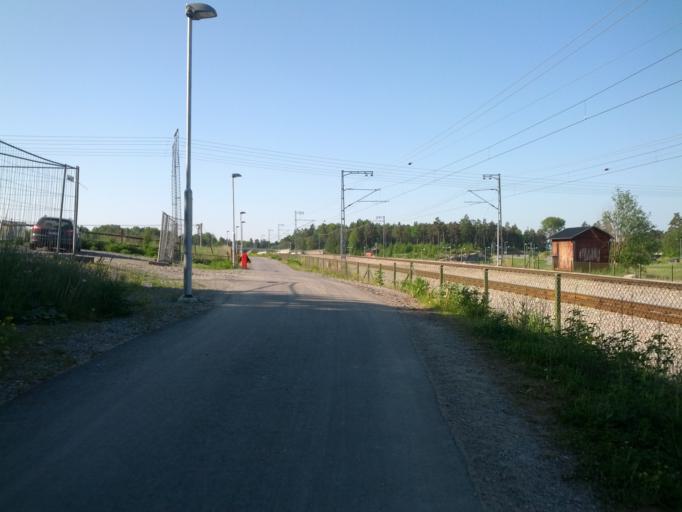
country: SE
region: Stockholm
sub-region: Taby Kommun
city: Taby
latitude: 59.4786
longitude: 18.0573
